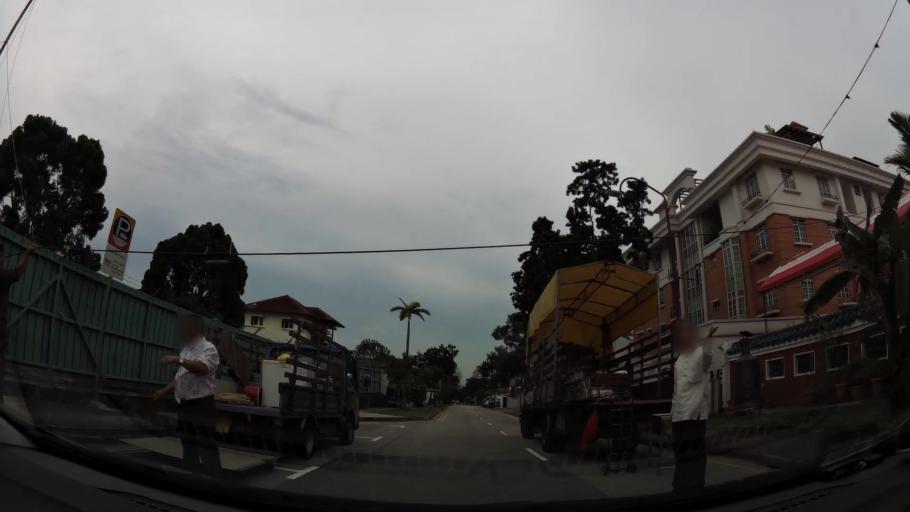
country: SG
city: Singapore
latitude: 1.3555
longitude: 103.8781
